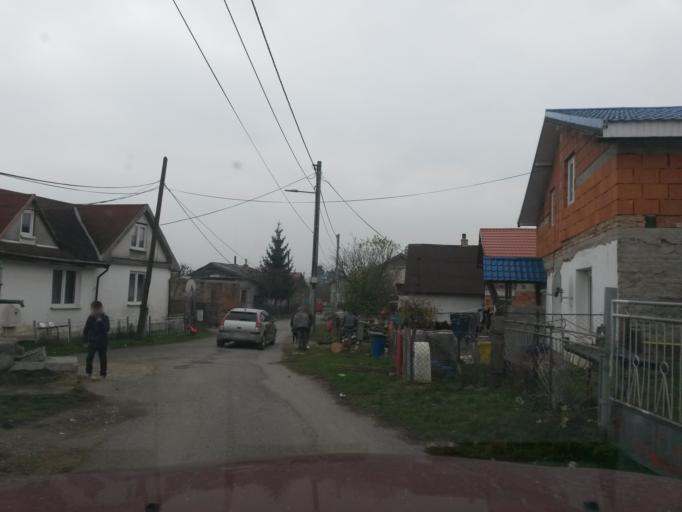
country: SK
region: Presovsky
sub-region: Okres Presov
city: Presov
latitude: 48.8814
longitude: 21.2754
